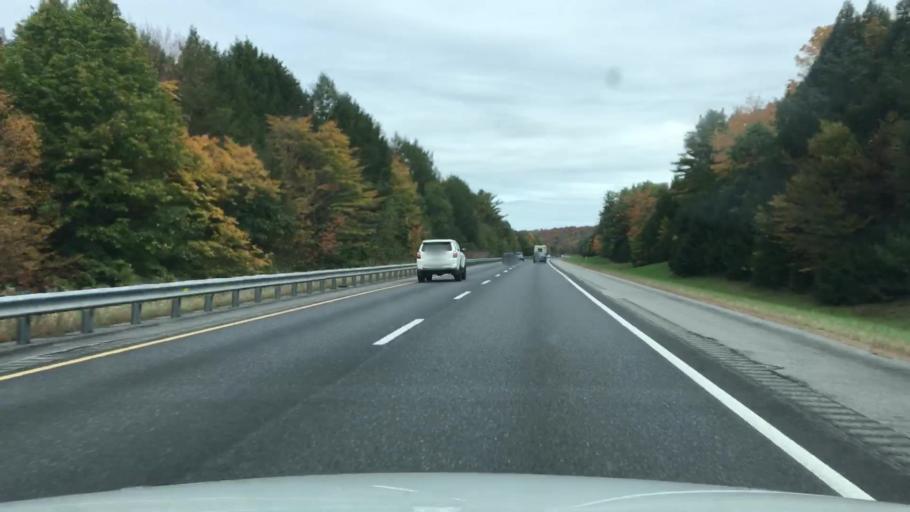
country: US
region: Maine
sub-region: Sagadahoc County
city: Richmond
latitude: 44.0569
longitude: -69.8863
